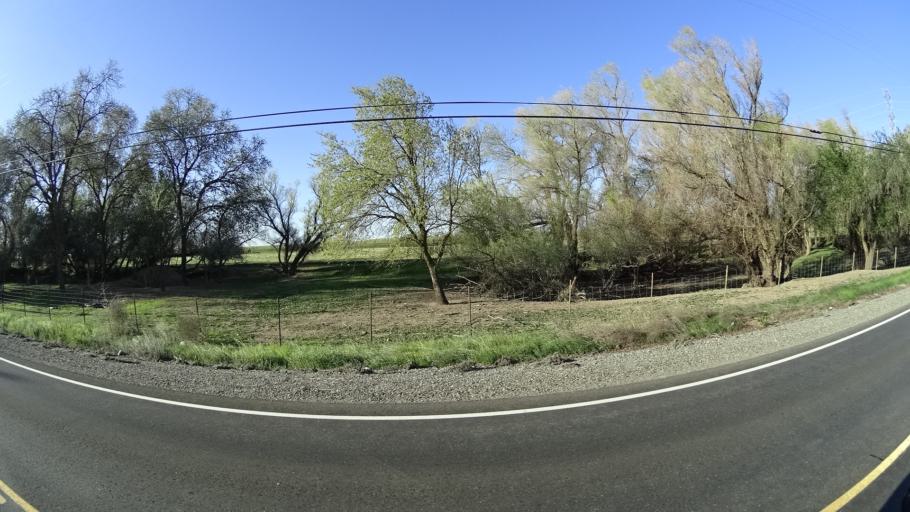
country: US
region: California
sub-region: Glenn County
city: Orland
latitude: 39.7750
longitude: -122.2724
